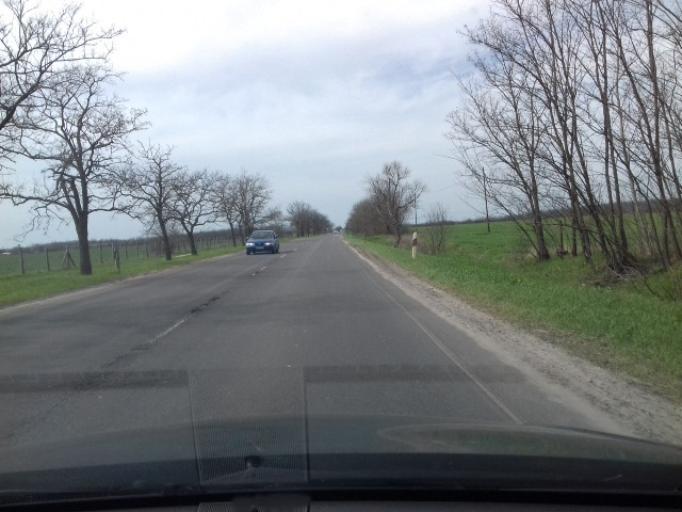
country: HU
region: Jasz-Nagykun-Szolnok
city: Kunszentmarton
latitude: 46.8476
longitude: 20.2571
